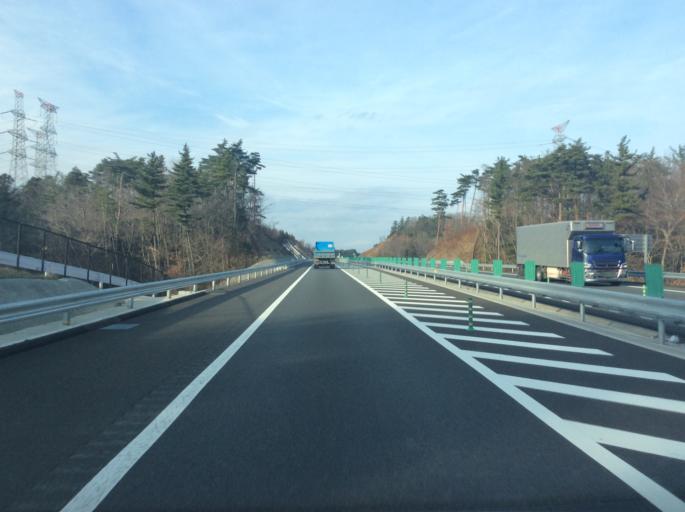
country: JP
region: Fukushima
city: Namie
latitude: 37.5253
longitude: 140.9426
